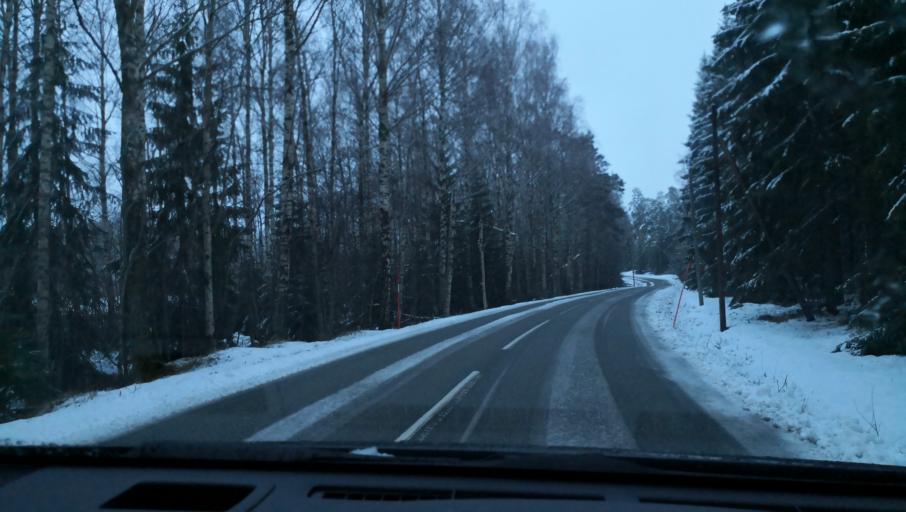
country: SE
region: Vaestmanland
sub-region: Kopings Kommun
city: Kolsva
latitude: 59.5819
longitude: 15.8037
